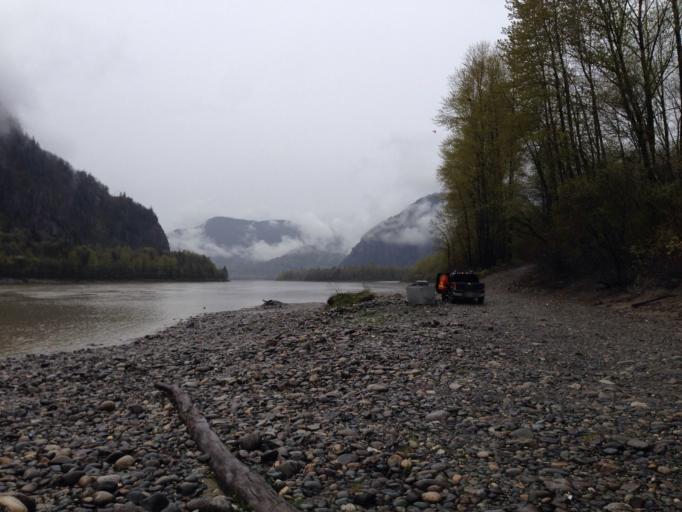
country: CA
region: British Columbia
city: Hope
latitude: 49.3671
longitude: -121.5491
